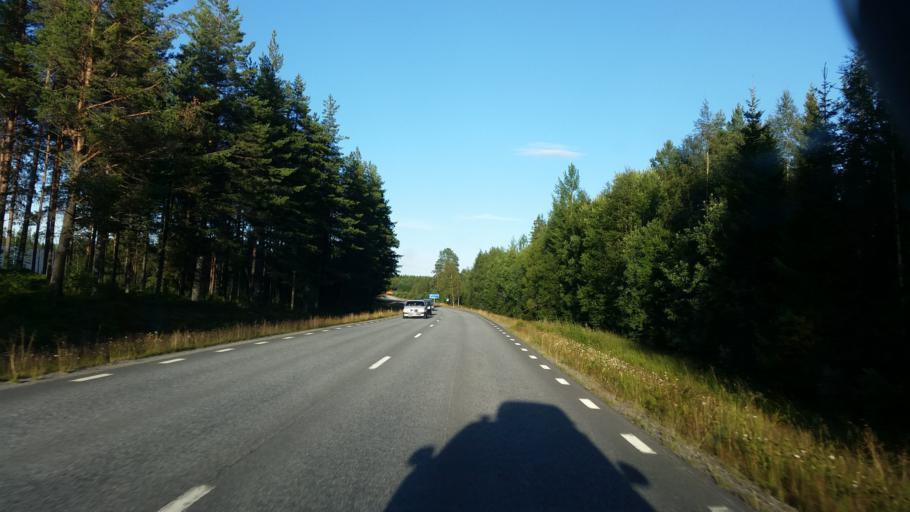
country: SE
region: Vaesterbotten
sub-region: Dorotea Kommun
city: Dorotea
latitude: 64.2537
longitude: 16.4650
